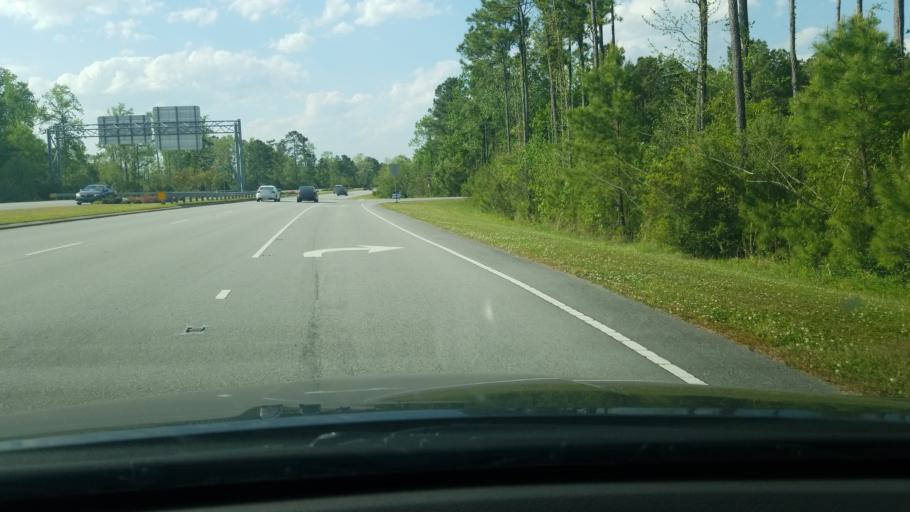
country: US
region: North Carolina
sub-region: Onslow County
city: Pumpkin Center
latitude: 34.7760
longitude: -77.4001
